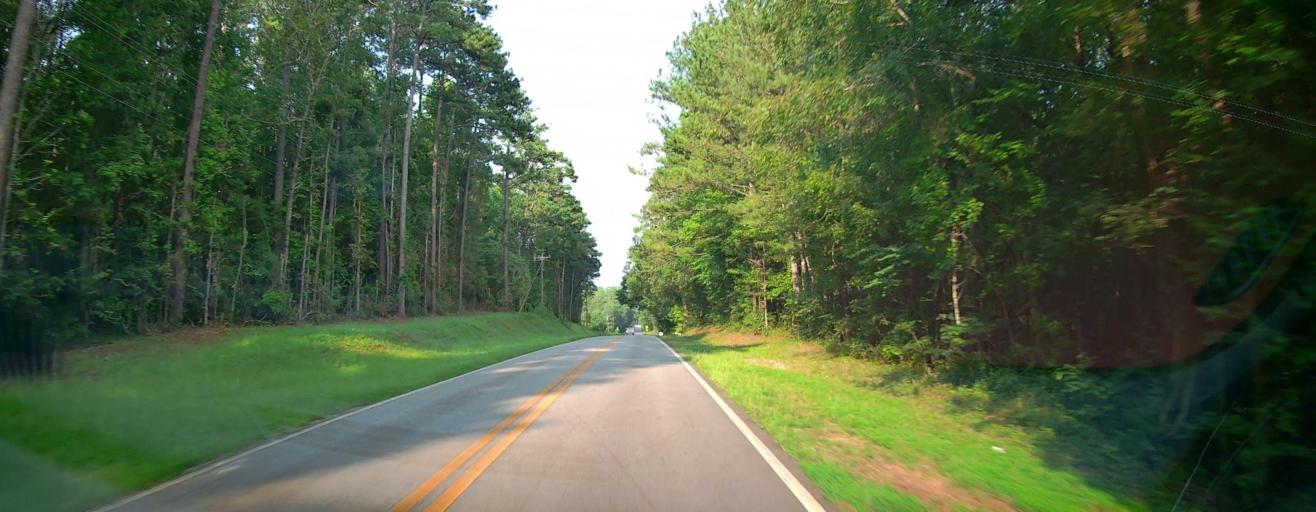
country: US
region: Georgia
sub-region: Monroe County
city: Forsyth
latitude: 33.1058
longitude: -83.8086
